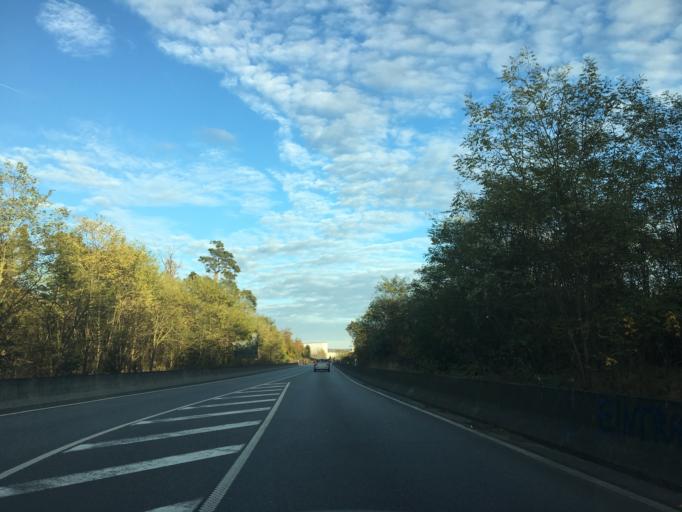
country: DE
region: Hesse
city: Pfungstadt
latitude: 49.8159
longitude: 8.6030
